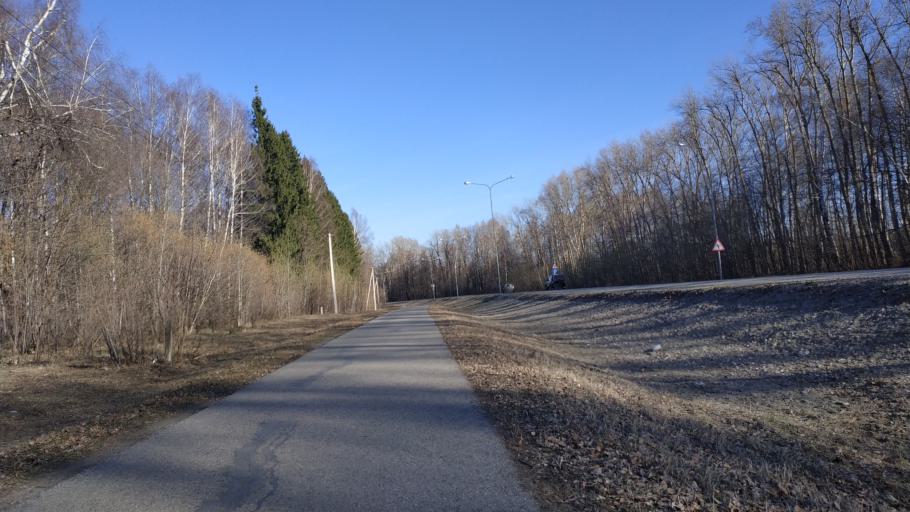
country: RU
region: Chuvashia
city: Novyye Lapsary
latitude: 56.1290
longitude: 47.1183
